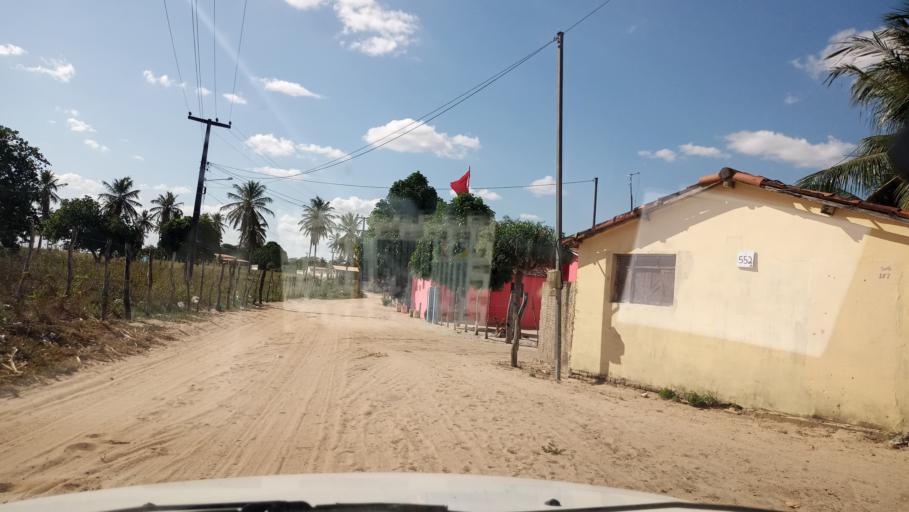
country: BR
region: Rio Grande do Norte
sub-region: Brejinho
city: Brejinho
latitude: -6.1731
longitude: -35.4678
